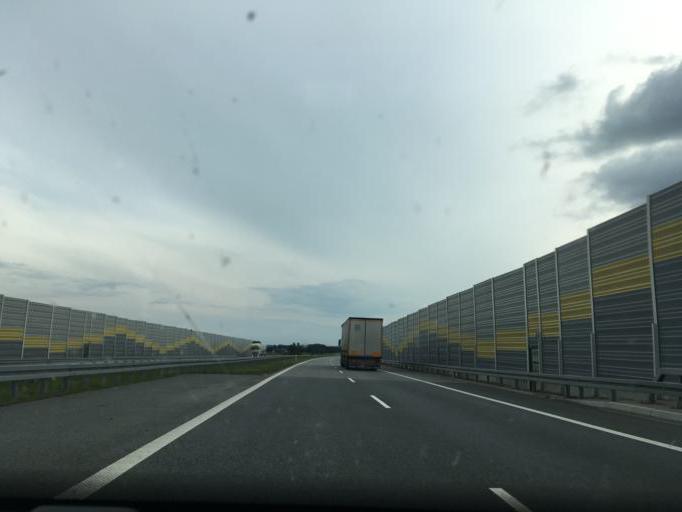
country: PL
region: Lodz Voivodeship
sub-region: Powiat sieradzki
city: Zloczew
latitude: 51.4202
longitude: 18.6437
